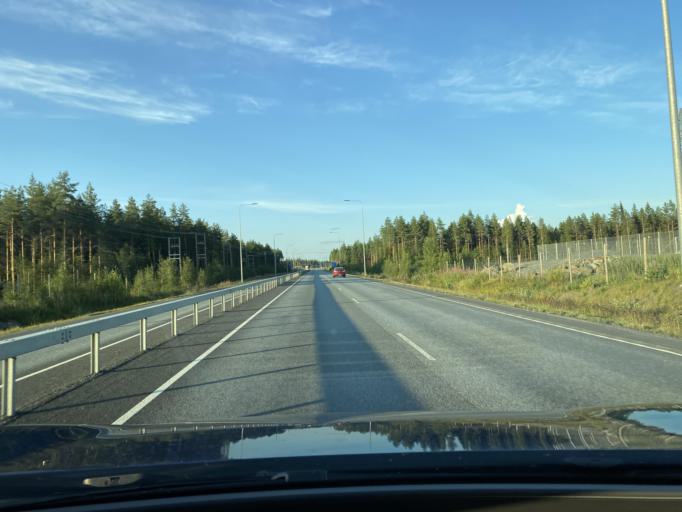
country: FI
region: Southern Ostrobothnia
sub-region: Seinaejoki
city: Seinaejoki
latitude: 62.7279
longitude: 22.8851
